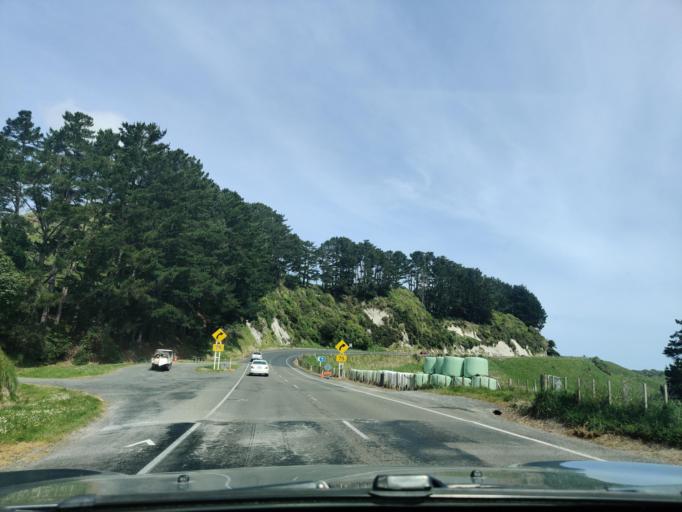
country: NZ
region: Taranaki
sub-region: South Taranaki District
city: Hawera
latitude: -39.6413
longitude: 174.3769
